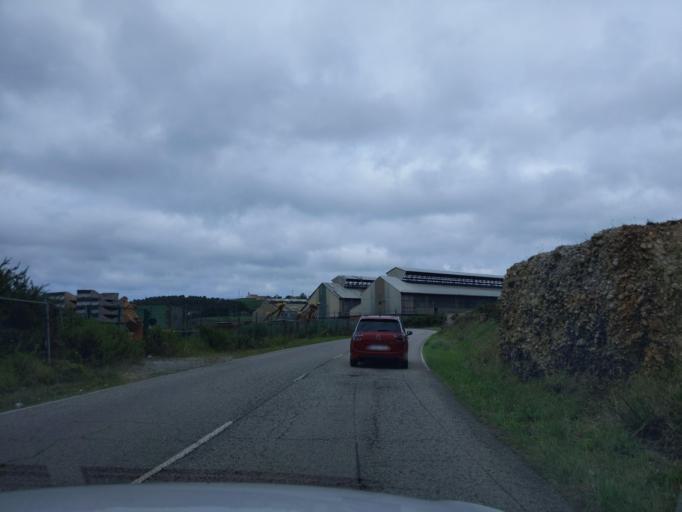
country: ES
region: Asturias
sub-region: Province of Asturias
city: Aviles
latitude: 43.5810
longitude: -5.9166
